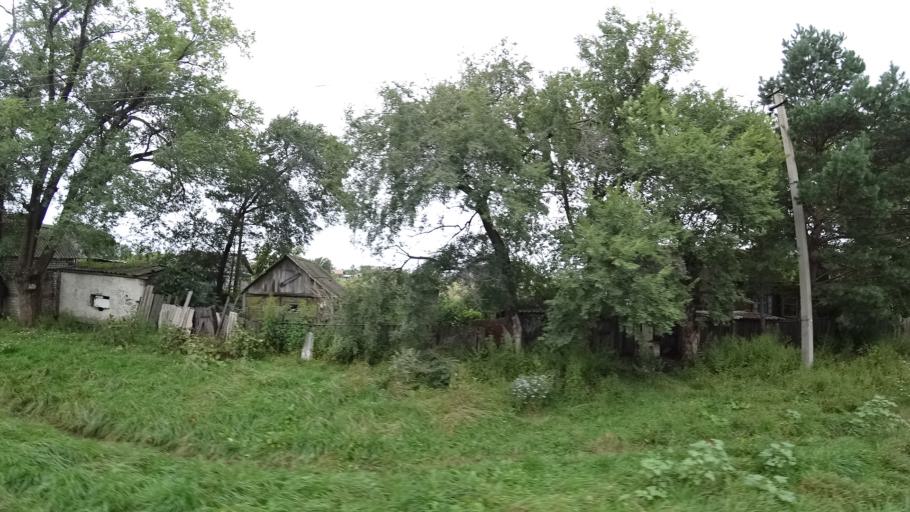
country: RU
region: Primorskiy
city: Chernigovka
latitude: 44.3394
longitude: 132.5621
